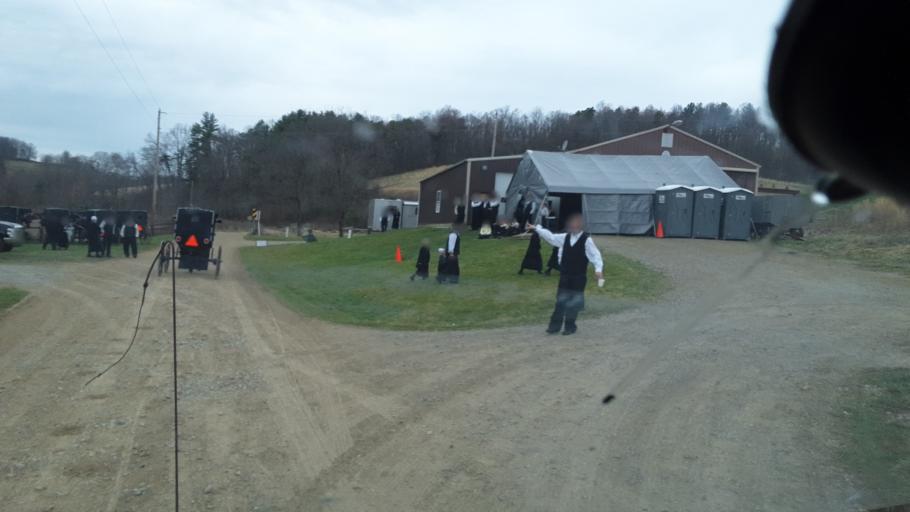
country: US
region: Ohio
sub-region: Coshocton County
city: West Lafayette
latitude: 40.3565
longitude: -81.7751
